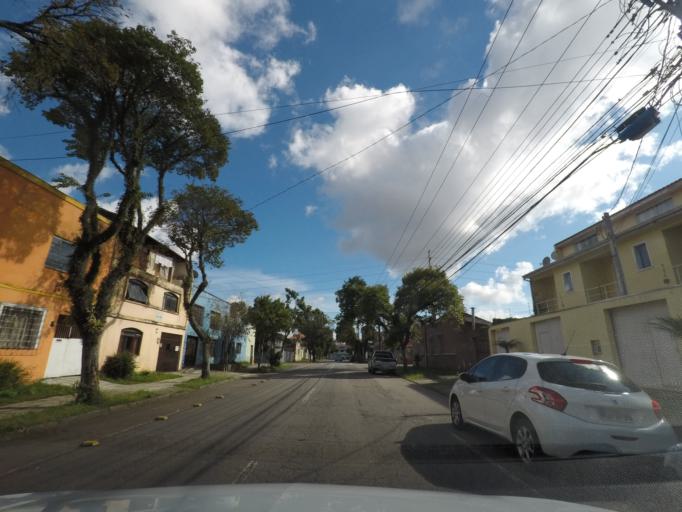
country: BR
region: Parana
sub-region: Curitiba
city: Curitiba
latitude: -25.4439
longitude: -49.2552
